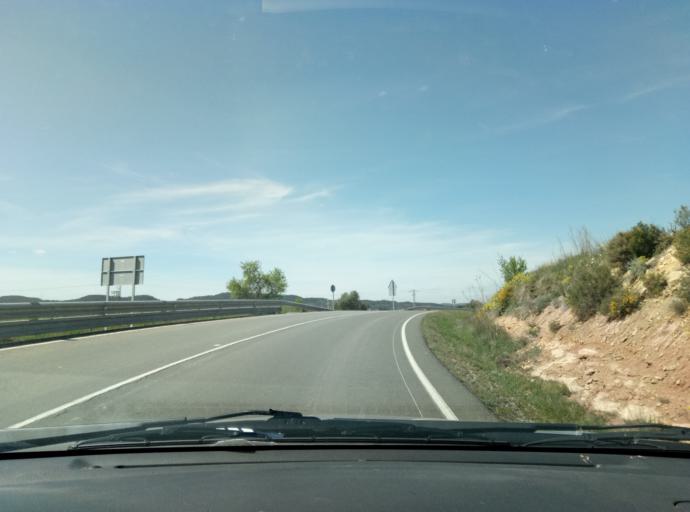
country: ES
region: Catalonia
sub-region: Provincia de Lleida
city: Vinaixa
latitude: 41.4223
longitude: 0.9256
